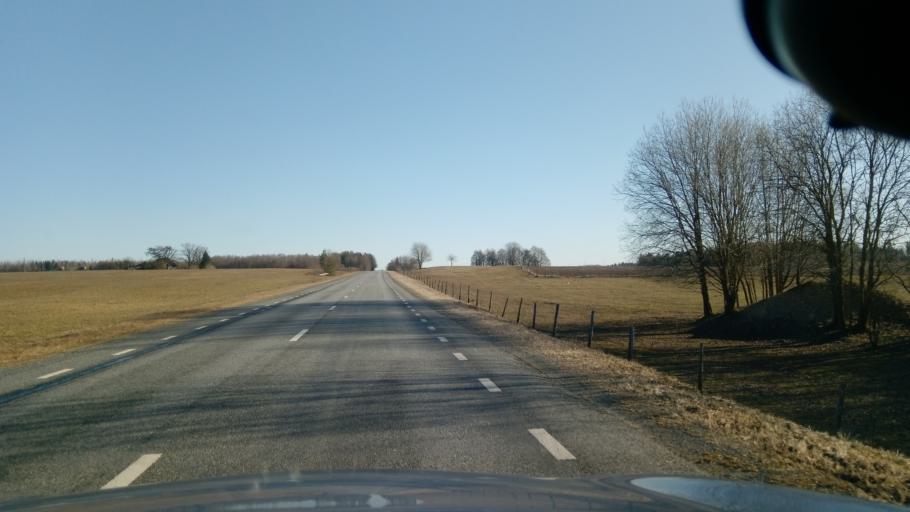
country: EE
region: Jaervamaa
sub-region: Jaerva-Jaani vald
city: Jarva-Jaani
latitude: 59.0820
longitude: 25.9648
